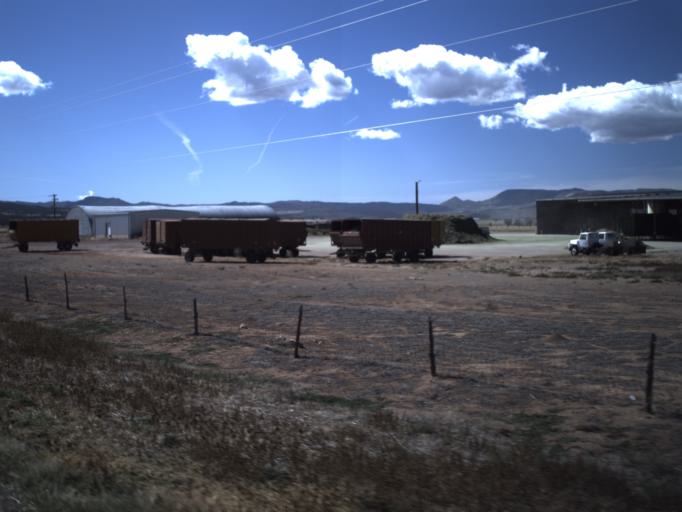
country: US
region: Utah
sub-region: Washington County
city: Enterprise
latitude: 37.6062
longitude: -113.6612
